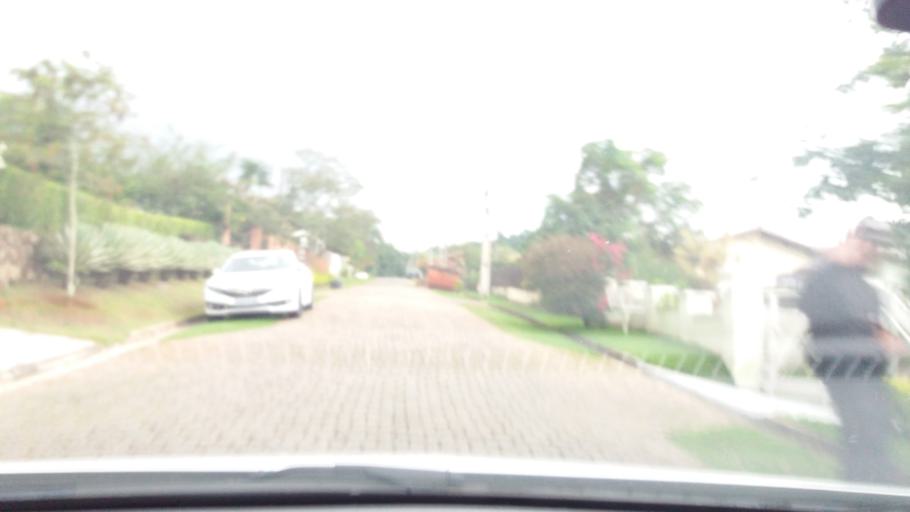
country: BR
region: Sao Paulo
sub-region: Bom Jesus Dos Perdoes
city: Bom Jesus dos Perdoes
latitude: -23.1715
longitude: -46.4557
